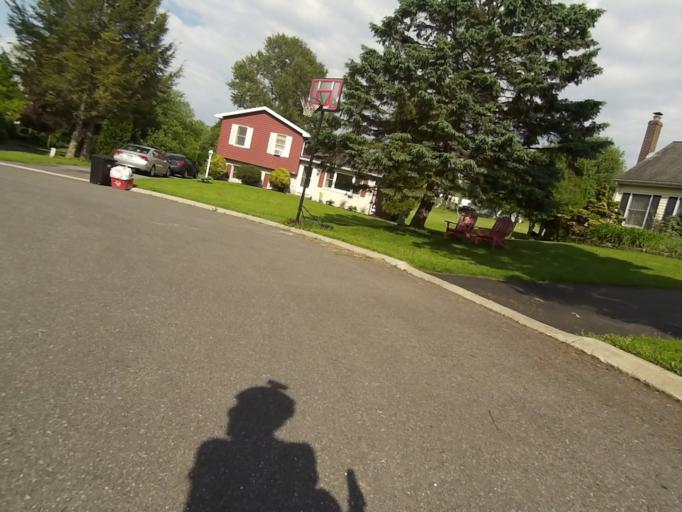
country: US
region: Pennsylvania
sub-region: Centre County
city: Houserville
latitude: 40.8277
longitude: -77.8308
